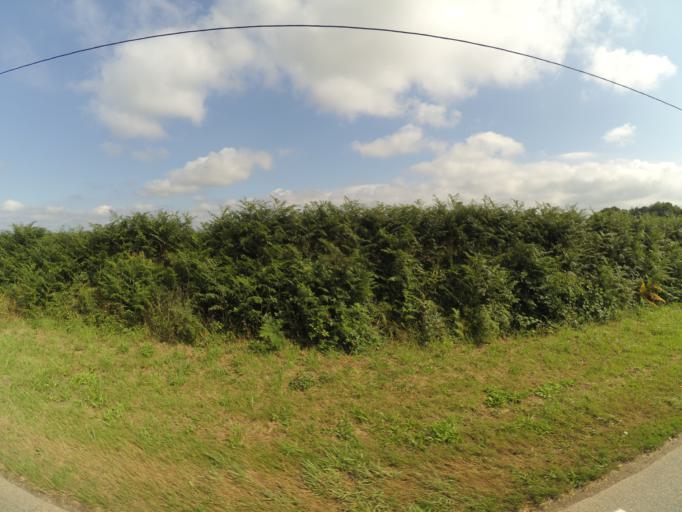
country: FR
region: Brittany
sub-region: Departement du Finistere
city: Le Trevoux
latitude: 47.9216
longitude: -3.6413
